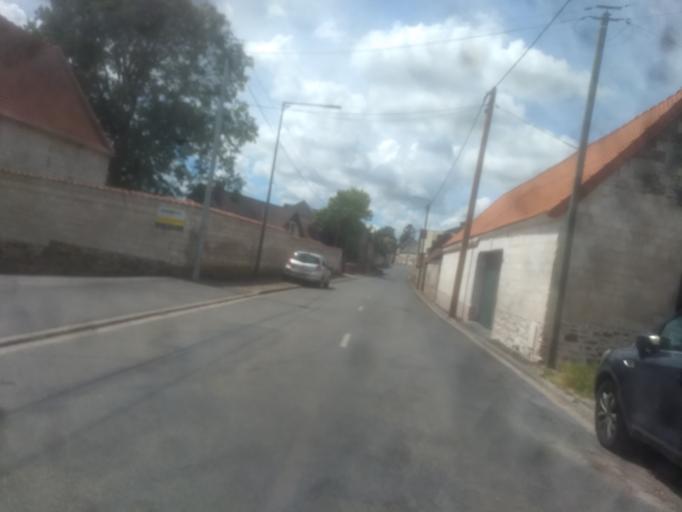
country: FR
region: Nord-Pas-de-Calais
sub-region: Departement du Pas-de-Calais
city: Mont-Saint-Eloi
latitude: 50.3470
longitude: 2.6579
